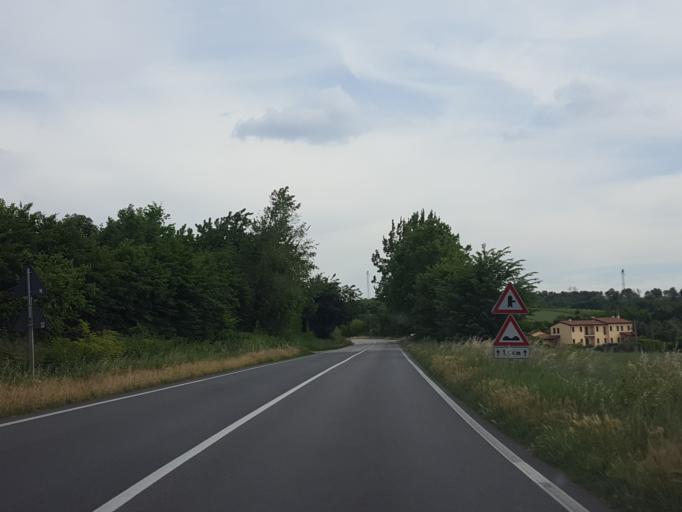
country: IT
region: Veneto
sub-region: Provincia di Vicenza
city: Alonte
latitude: 45.3542
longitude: 11.4430
